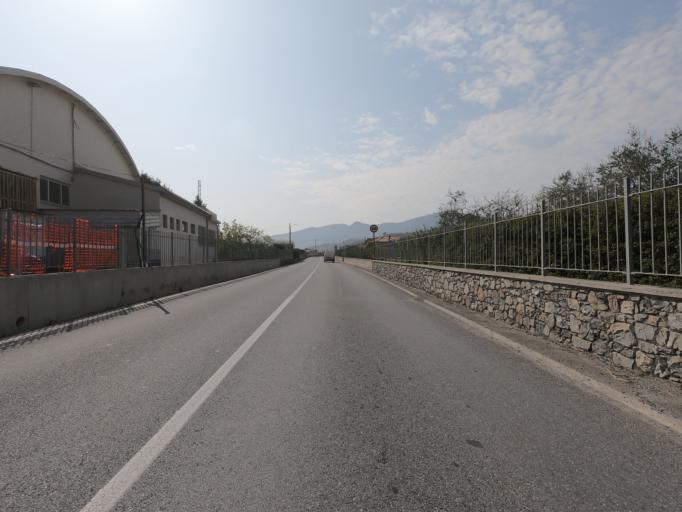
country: IT
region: Liguria
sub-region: Provincia di Savona
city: Cisano
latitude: 44.0789
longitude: 8.1570
